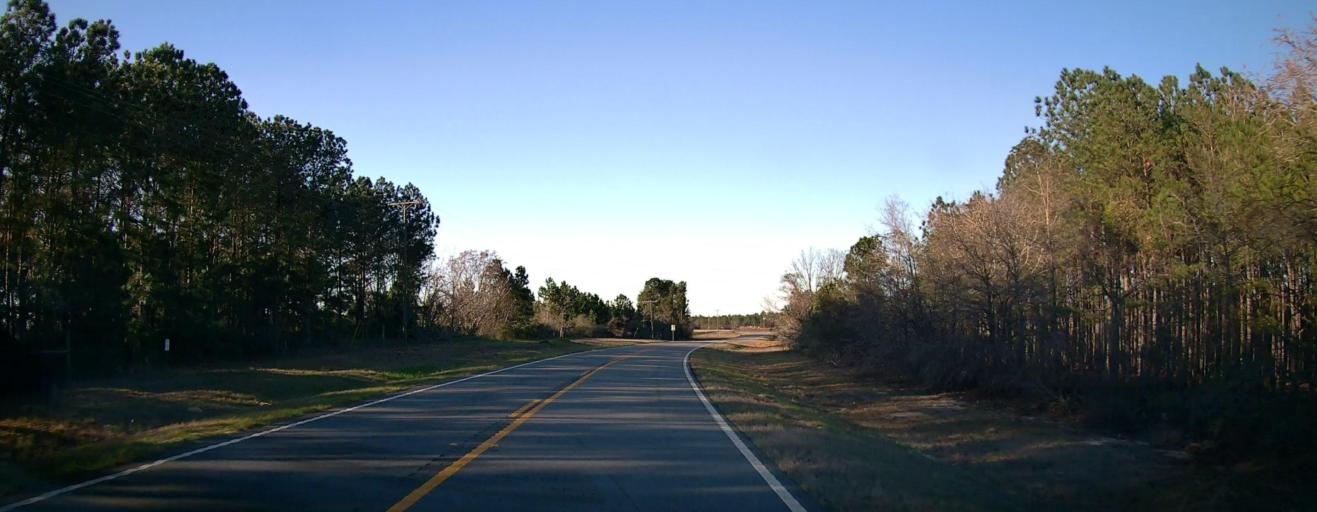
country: US
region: Georgia
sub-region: Talbot County
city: Talbotton
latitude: 32.5569
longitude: -84.4374
